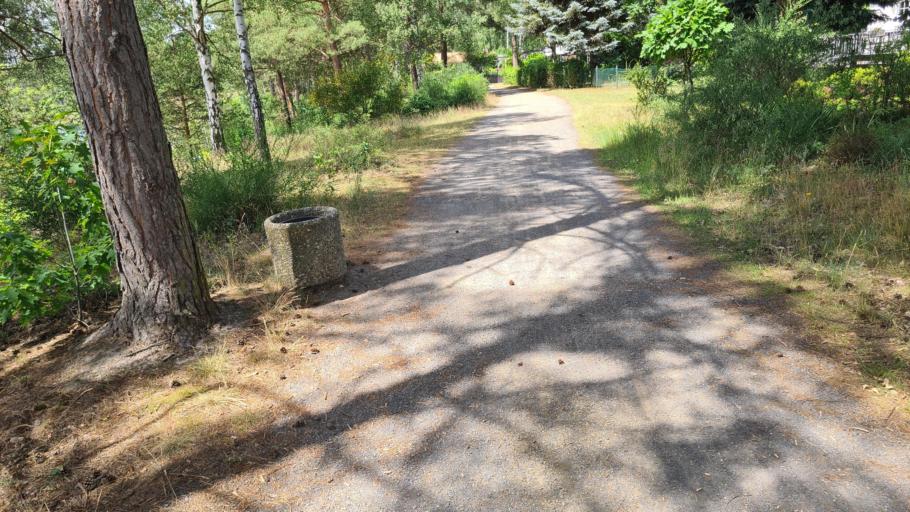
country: DE
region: Brandenburg
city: Plessa
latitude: 51.5192
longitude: 13.6592
